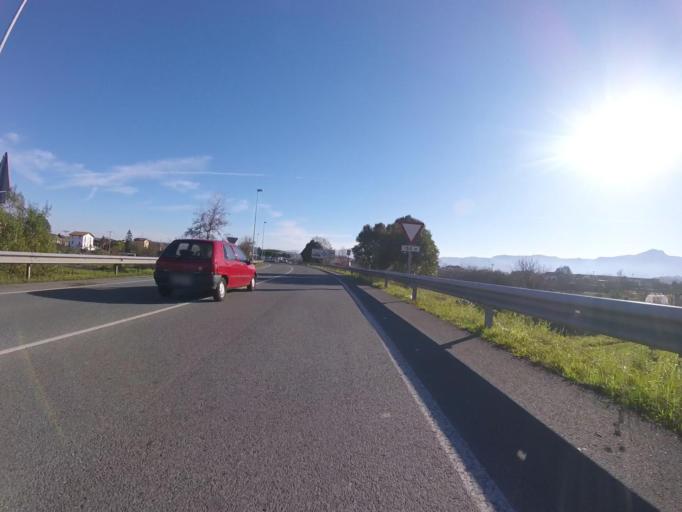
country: ES
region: Basque Country
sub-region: Provincia de Guipuzcoa
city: Fuenterrabia
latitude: 43.3600
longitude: -1.7942
